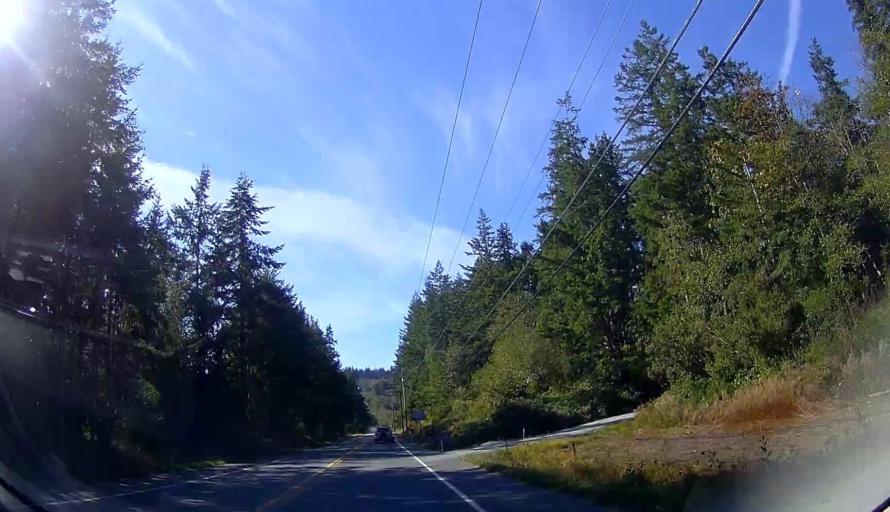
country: US
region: Washington
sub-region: Island County
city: Camano
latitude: 48.2318
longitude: -122.4748
